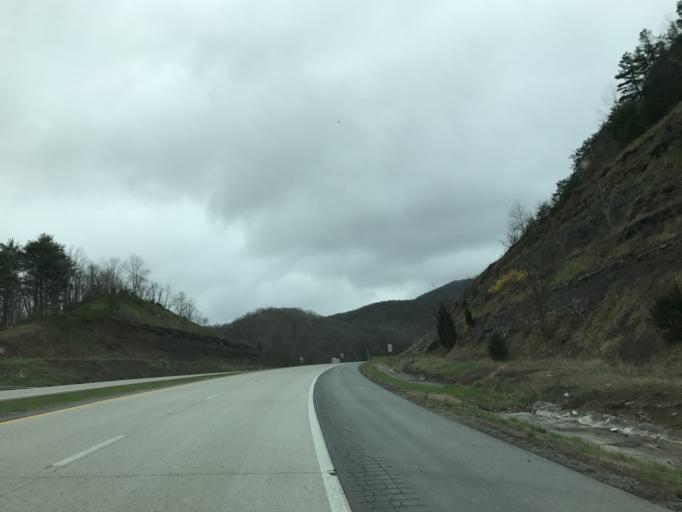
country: US
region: West Virginia
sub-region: Summers County
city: Hinton
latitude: 37.7857
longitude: -80.8862
